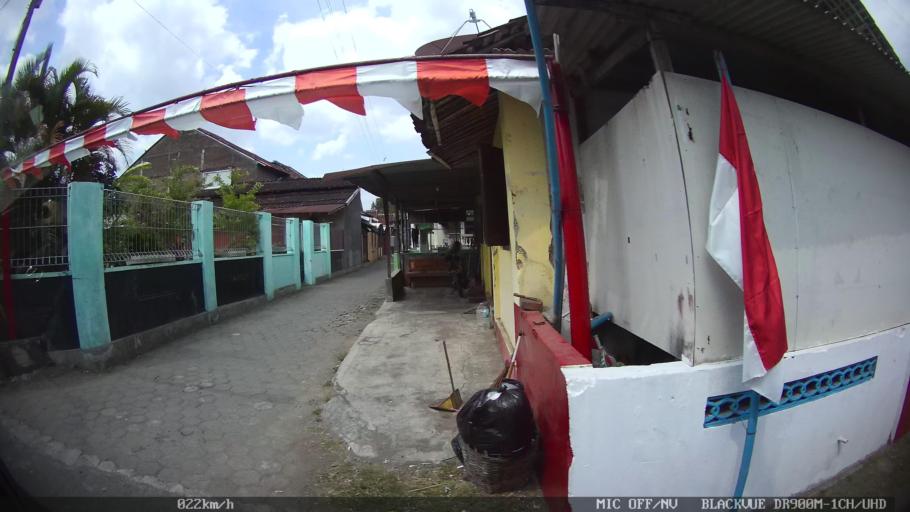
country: ID
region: Daerah Istimewa Yogyakarta
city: Kasihan
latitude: -7.8189
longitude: 110.3383
